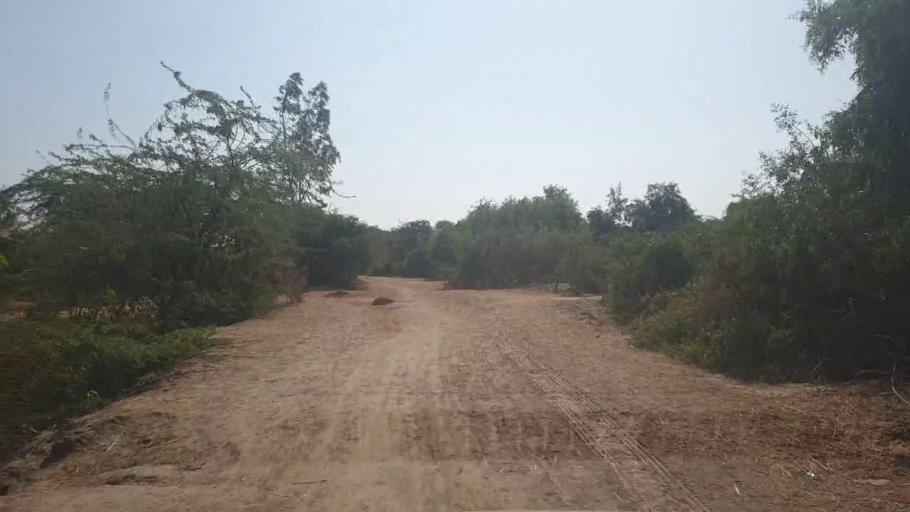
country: PK
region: Sindh
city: Badin
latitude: 24.7150
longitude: 68.8990
